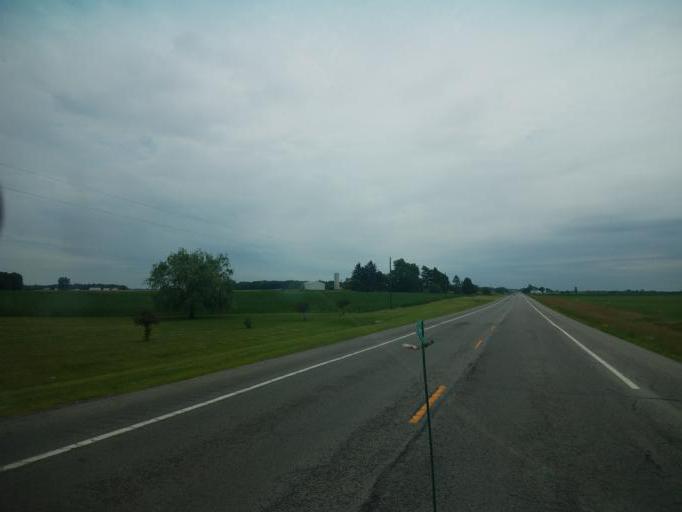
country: US
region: Ohio
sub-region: Hardin County
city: Kenton
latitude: 40.6783
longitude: -83.6733
